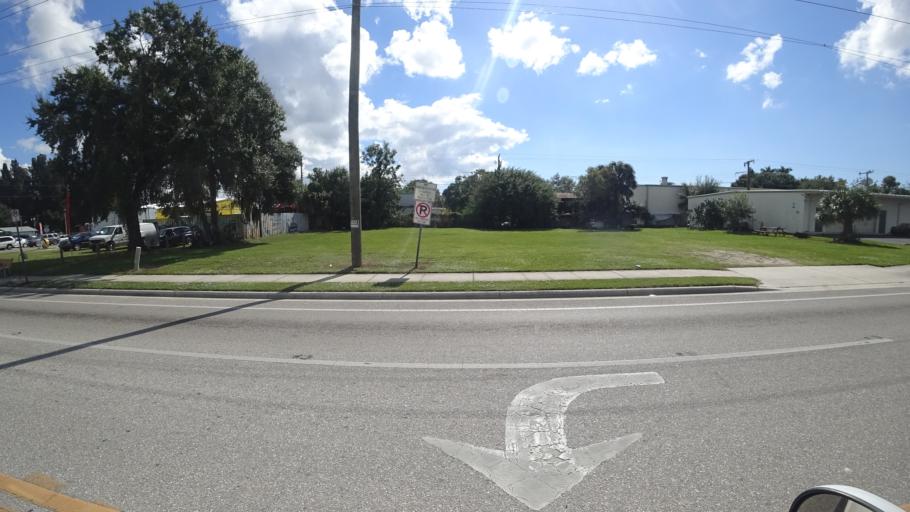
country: US
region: Florida
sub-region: Manatee County
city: South Bradenton
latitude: 27.4739
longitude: -82.5718
